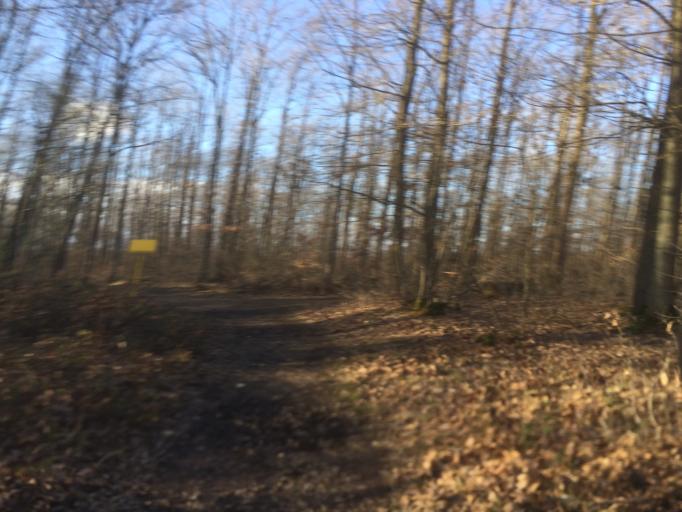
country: FR
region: Ile-de-France
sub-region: Departement de l'Essonne
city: Igny
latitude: 48.7411
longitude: 2.2198
